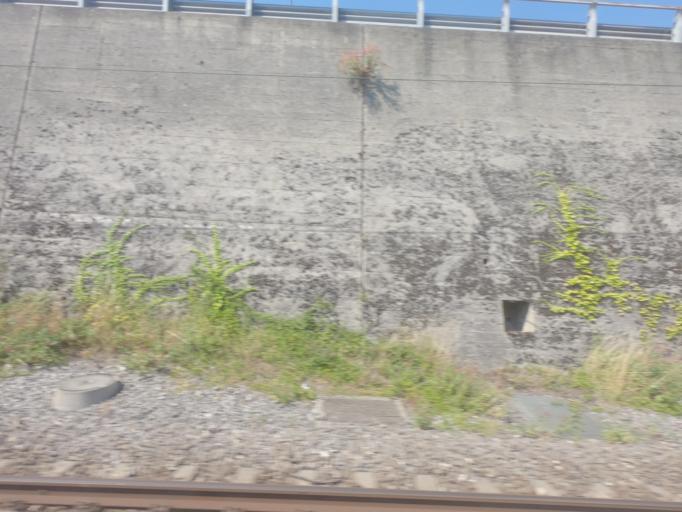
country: CH
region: Vaud
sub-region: Riviera-Pays-d'Enhaut District
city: Chardonne
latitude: 46.4705
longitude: 6.8132
